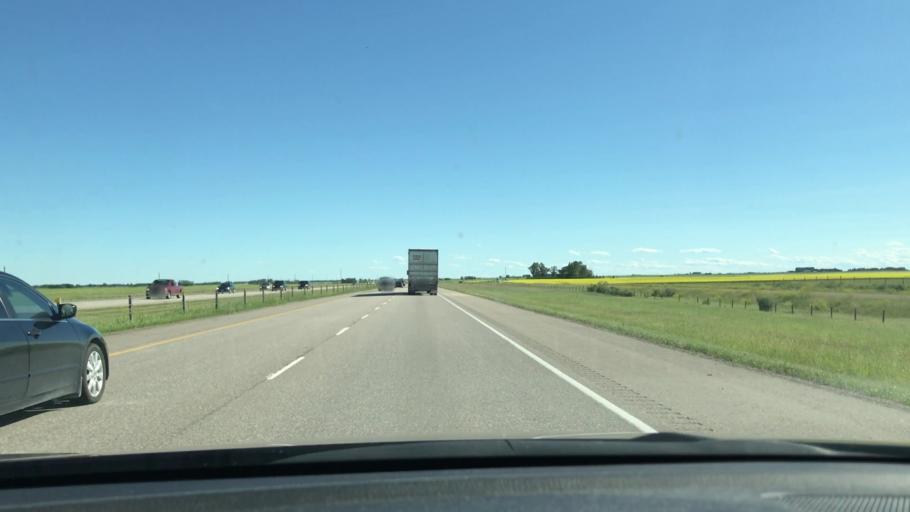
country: CA
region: Alberta
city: Olds
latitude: 51.7185
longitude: -114.0256
